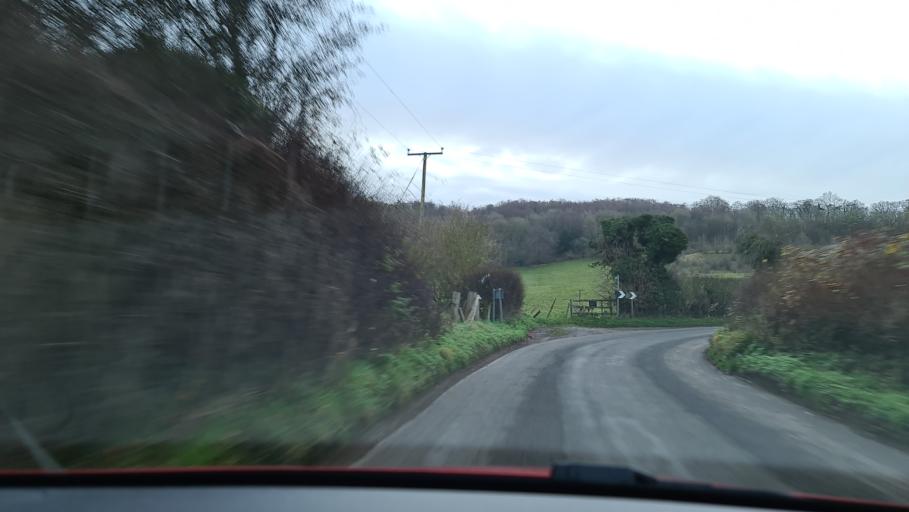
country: GB
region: England
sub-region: Buckinghamshire
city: Princes Risborough
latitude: 51.7141
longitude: -0.8125
